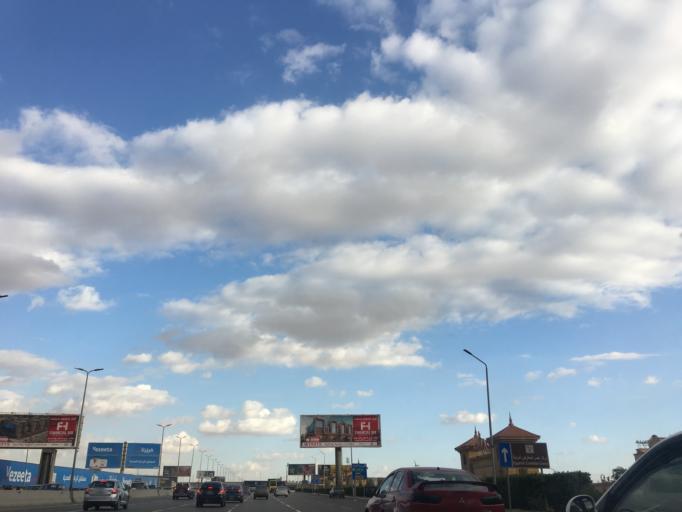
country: EG
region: Muhafazat al Qahirah
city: Cairo
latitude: 30.0242
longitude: 31.3632
